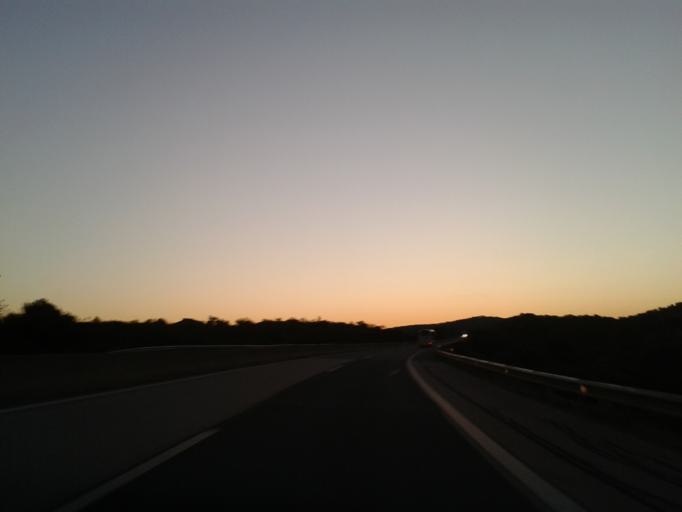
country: PT
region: Faro
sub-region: Loule
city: Boliqueime
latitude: 37.1620
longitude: -8.1932
